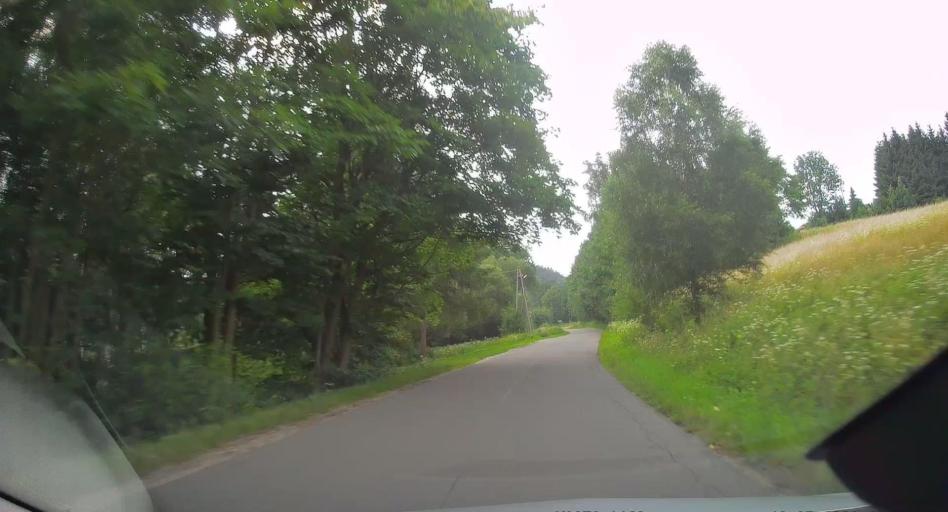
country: PL
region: Lower Silesian Voivodeship
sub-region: Powiat klodzki
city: Ludwikowice Klodzkie
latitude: 50.6498
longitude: 16.4728
